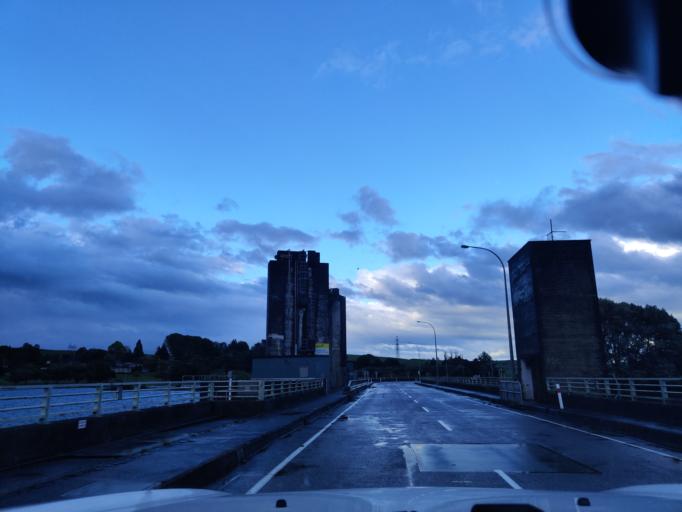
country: NZ
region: Waikato
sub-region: South Waikato District
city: Tokoroa
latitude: -38.4199
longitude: 175.8082
